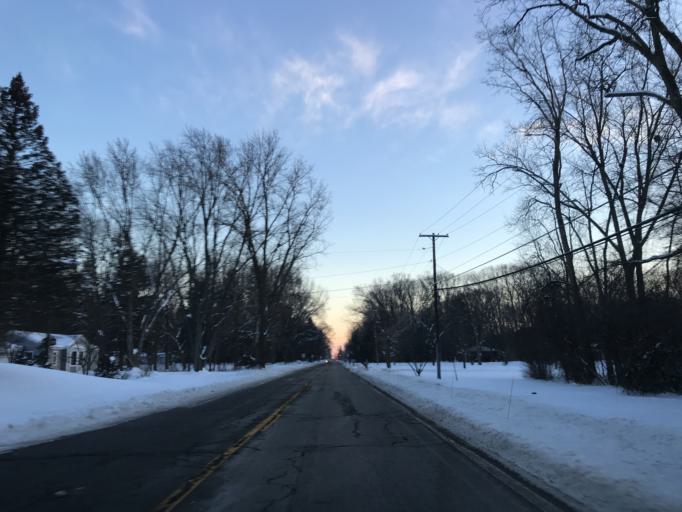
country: US
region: Michigan
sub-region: Oakland County
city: Bingham Farms
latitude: 42.4637
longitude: -83.2984
